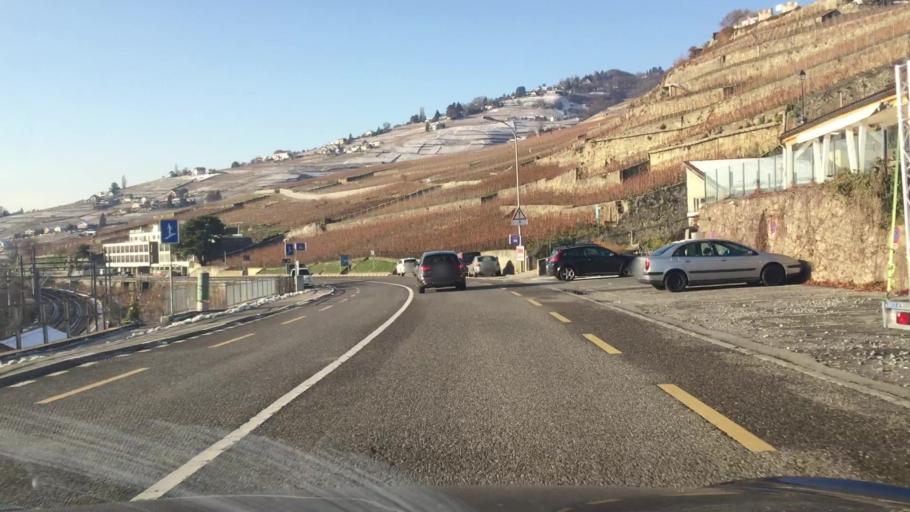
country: CH
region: Vaud
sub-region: Lavaux-Oron District
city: Cully
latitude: 46.4893
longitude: 6.7458
